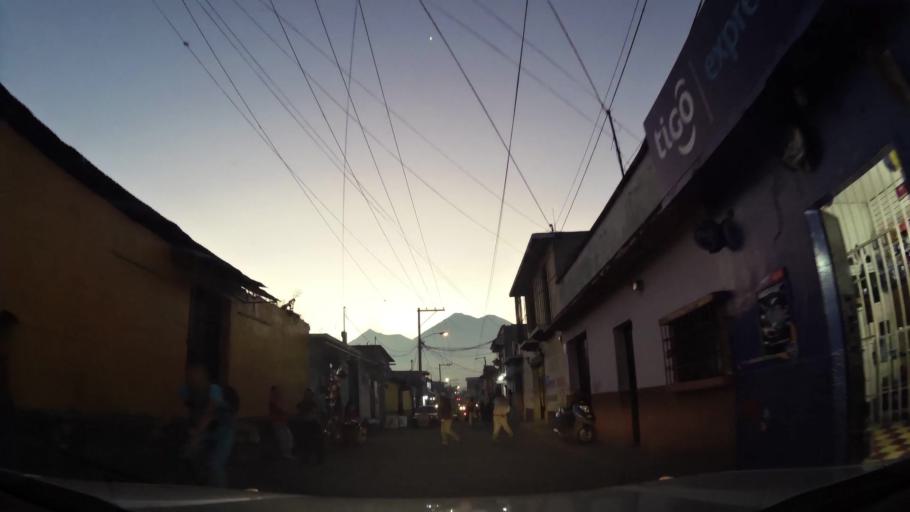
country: GT
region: Sacatepequez
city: Ciudad Vieja
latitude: 14.5239
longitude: -90.7632
